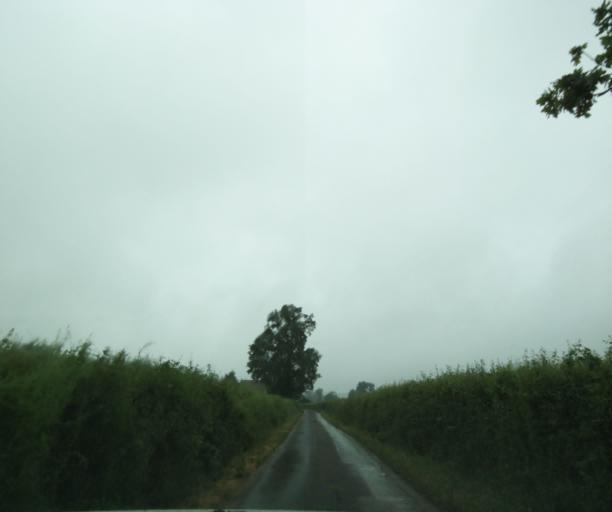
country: FR
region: Bourgogne
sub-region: Departement de Saone-et-Loire
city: Charolles
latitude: 46.3994
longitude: 4.2380
